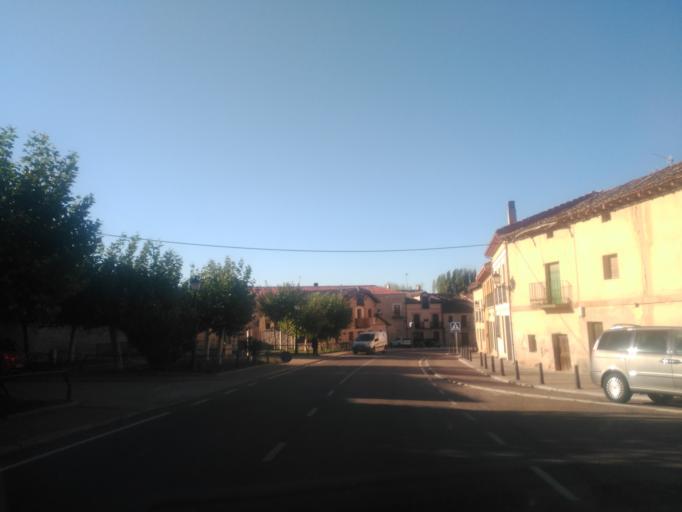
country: ES
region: Castille and Leon
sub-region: Provincia de Burgos
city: Penaranda de Duero
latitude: 41.6893
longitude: -3.4775
